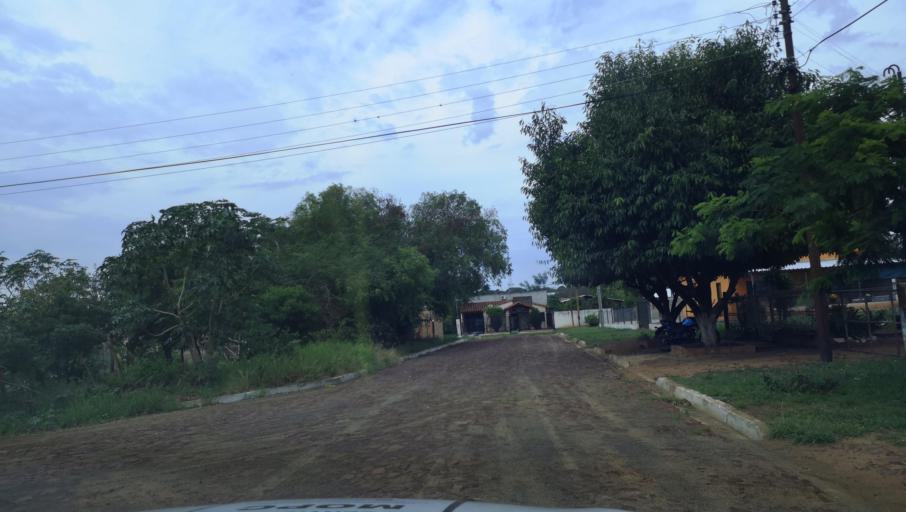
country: PY
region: Misiones
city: Santa Maria
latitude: -26.8799
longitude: -57.0271
